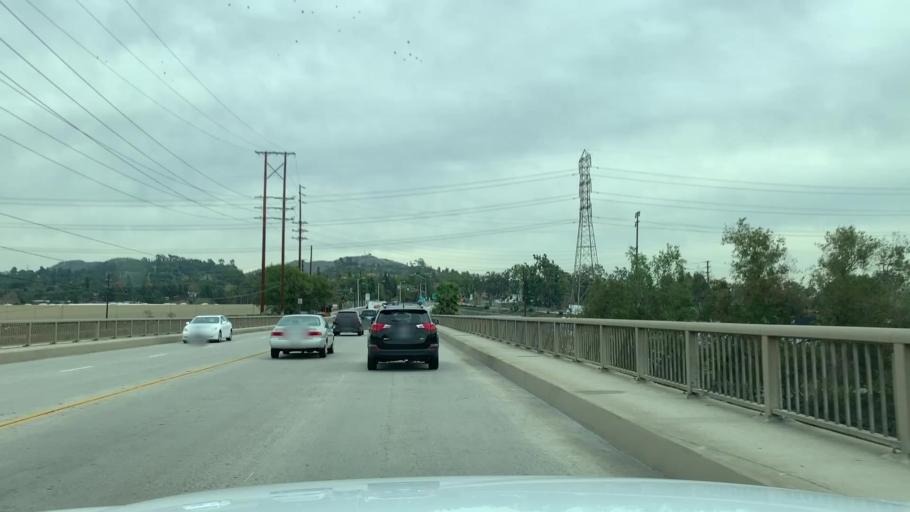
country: US
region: California
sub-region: Los Angeles County
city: West Whittier-Los Nietos
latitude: 34.0068
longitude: -118.0691
